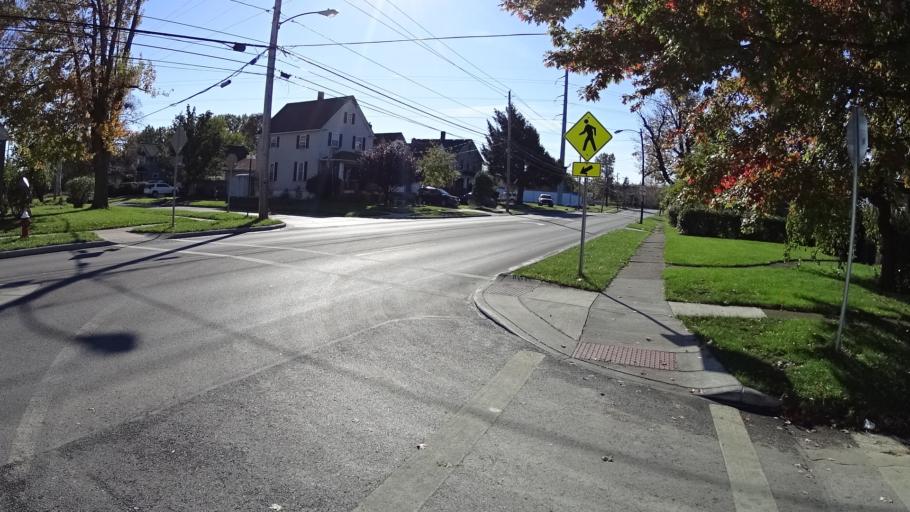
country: US
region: Ohio
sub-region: Lorain County
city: Lorain
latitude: 41.4398
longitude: -82.1610
